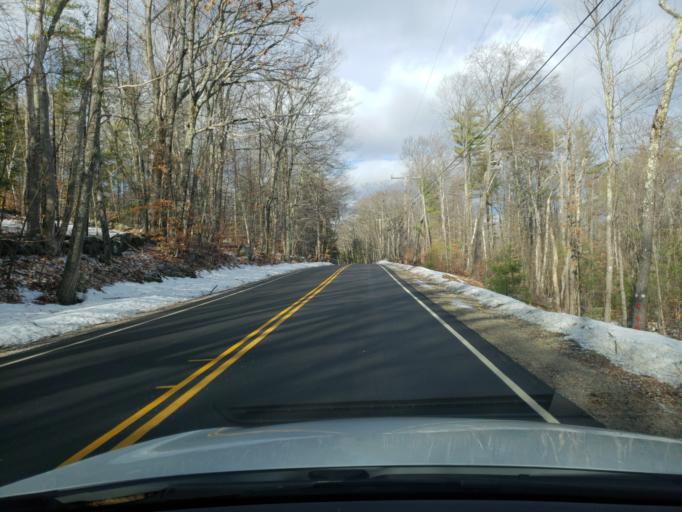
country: US
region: New Hampshire
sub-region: Hillsborough County
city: Greenfield
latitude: 43.0049
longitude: -71.8339
